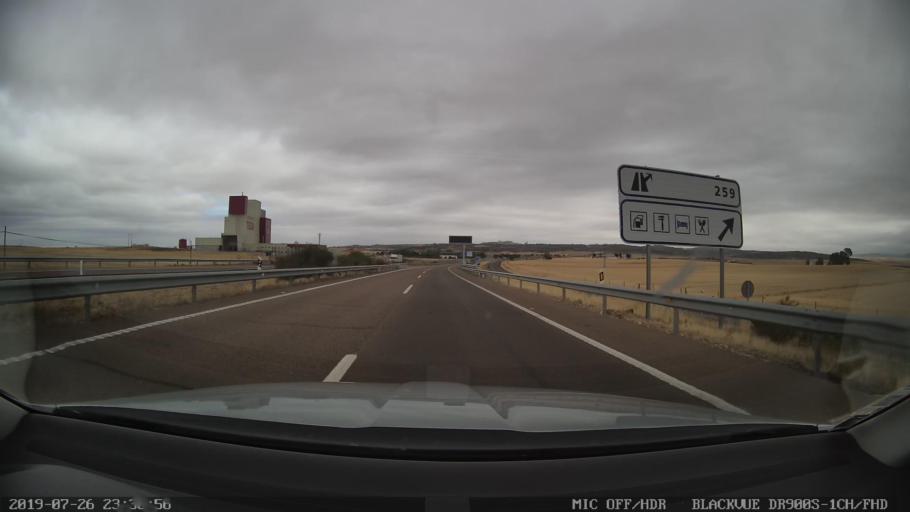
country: ES
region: Extremadura
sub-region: Provincia de Caceres
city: Trujillo
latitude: 39.4038
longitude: -5.8897
